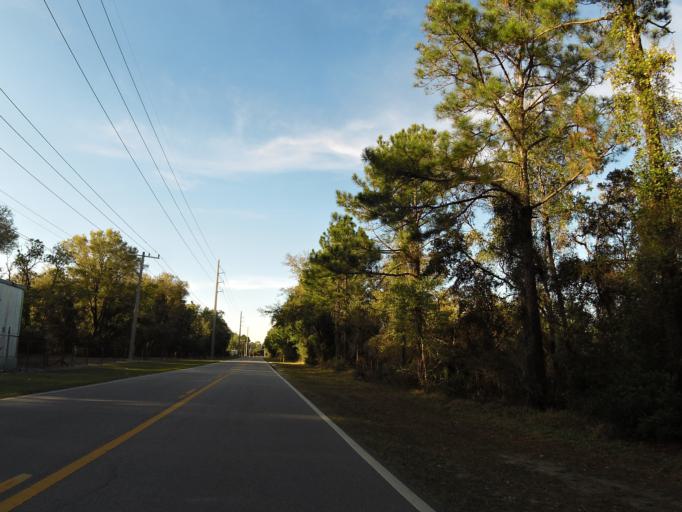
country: US
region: Florida
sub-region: Duval County
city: Jacksonville
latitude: 30.4359
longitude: -81.6041
